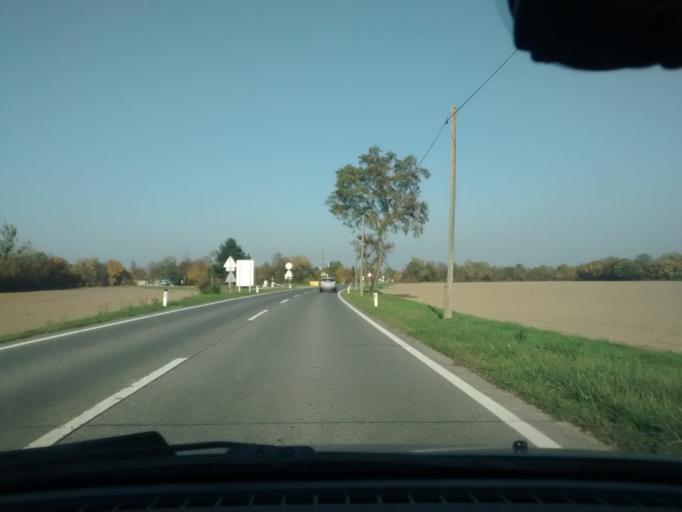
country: AT
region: Lower Austria
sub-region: Politischer Bezirk Modling
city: Achau
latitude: 48.0754
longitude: 16.3871
